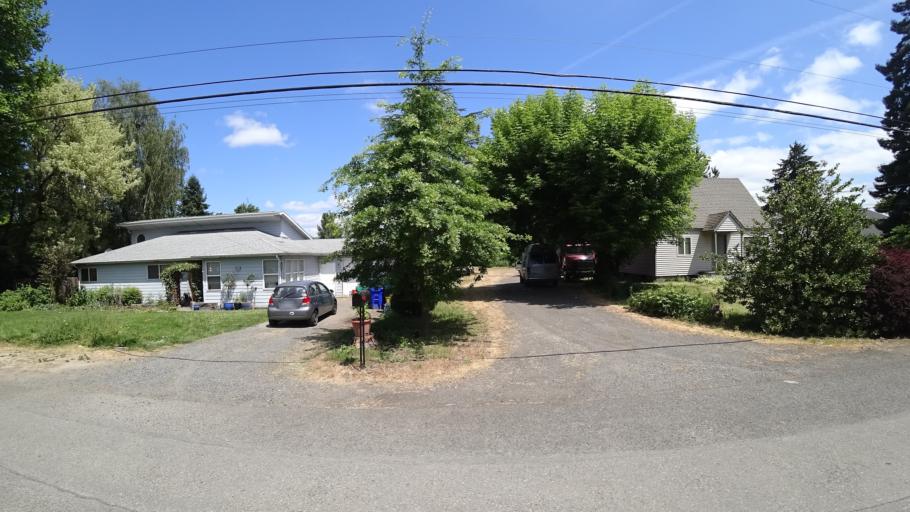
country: US
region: Washington
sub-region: Clark County
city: Vancouver
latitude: 45.5986
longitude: -122.6626
